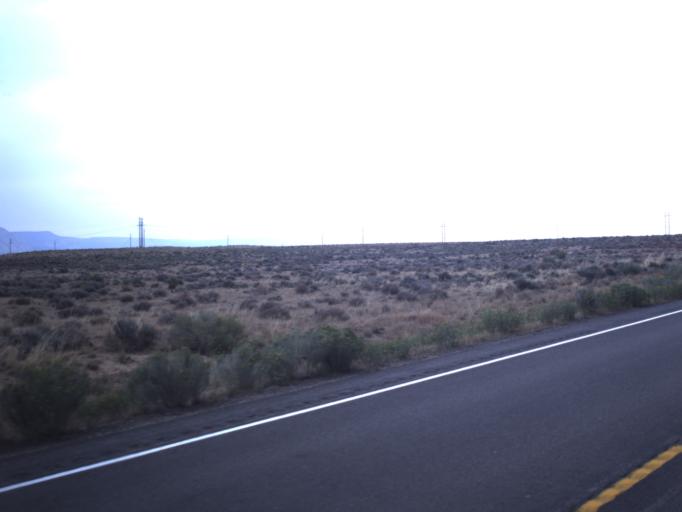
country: US
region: Utah
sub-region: Uintah County
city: Naples
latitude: 40.2264
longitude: -109.4004
